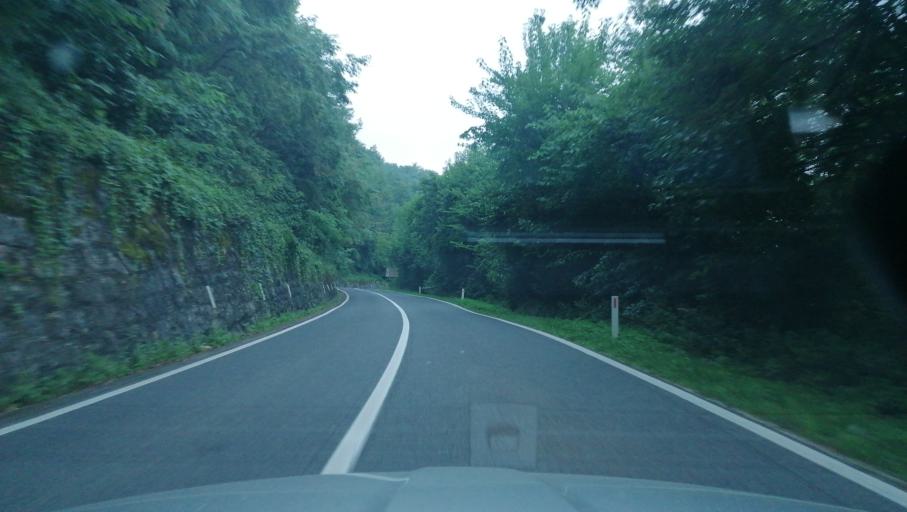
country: BA
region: Federation of Bosnia and Herzegovina
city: Jablanica
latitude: 43.7158
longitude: 17.7133
